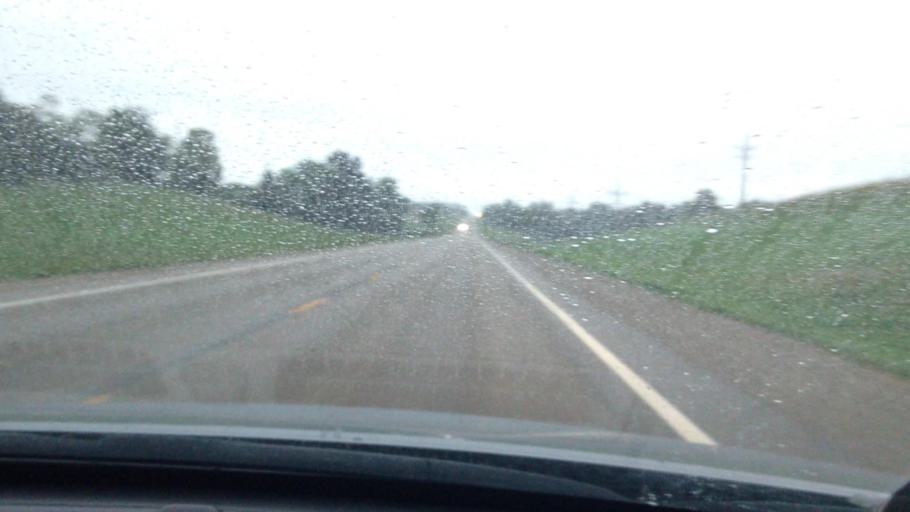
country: US
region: Kansas
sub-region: Brown County
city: Hiawatha
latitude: 39.8298
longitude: -95.5270
